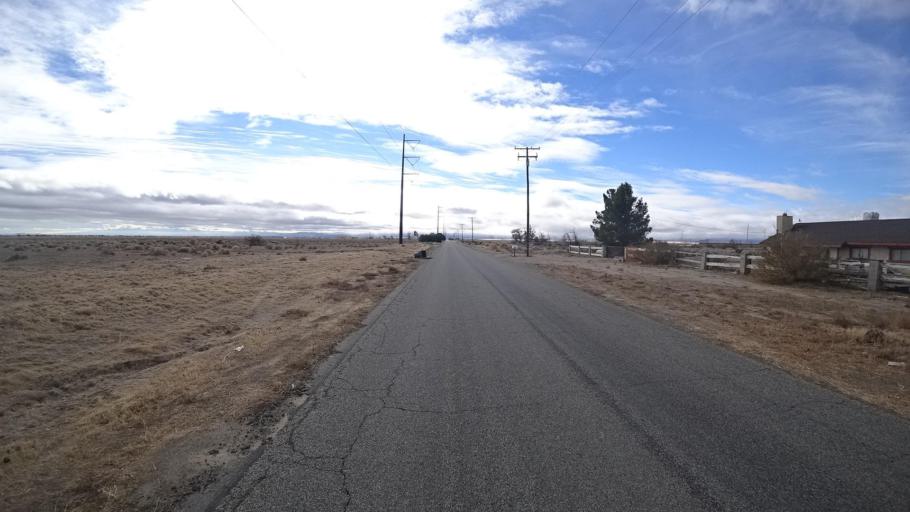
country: US
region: California
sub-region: Kern County
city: Rosamond
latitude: 34.8499
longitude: -118.3089
